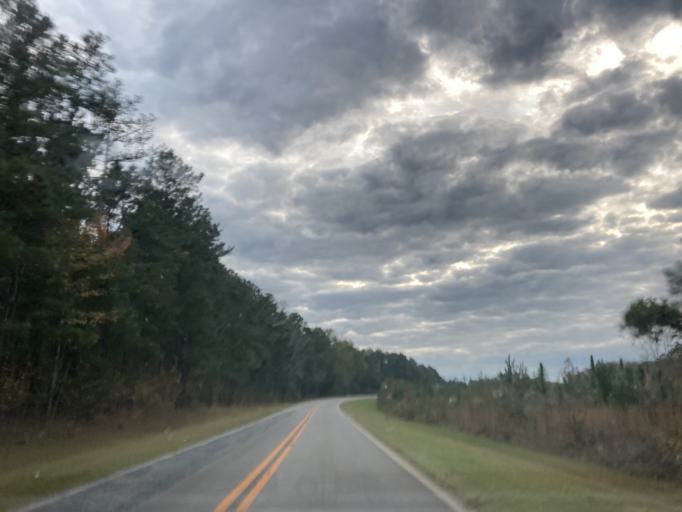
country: US
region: Georgia
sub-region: Jones County
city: Gray
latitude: 32.9558
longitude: -83.5085
